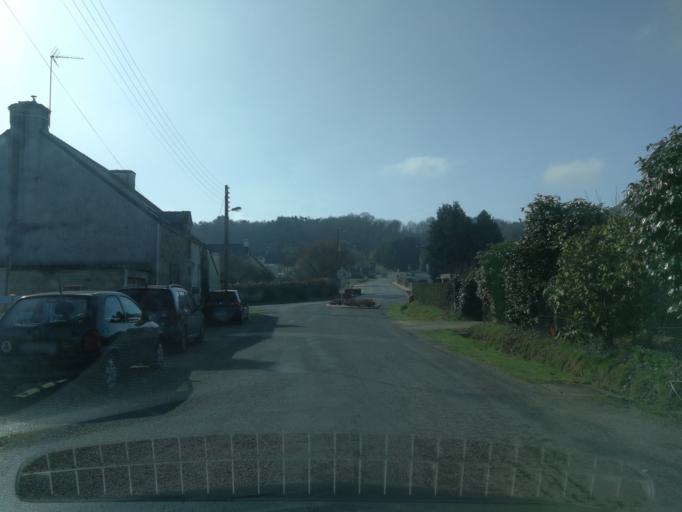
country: FR
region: Brittany
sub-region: Departement du Morbihan
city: La Vraie-Croix
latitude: 47.7109
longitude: -2.5182
